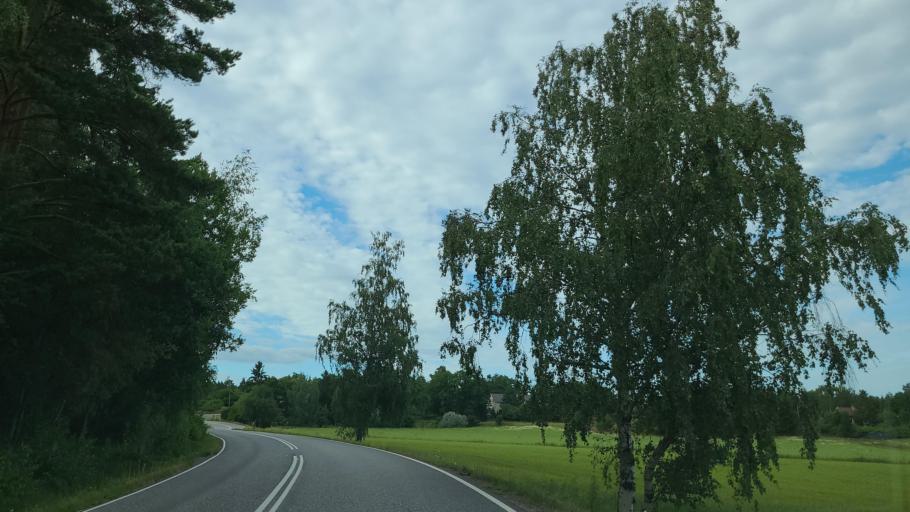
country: FI
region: Varsinais-Suomi
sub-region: Turku
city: Rymaettylae
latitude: 60.3517
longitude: 21.9586
